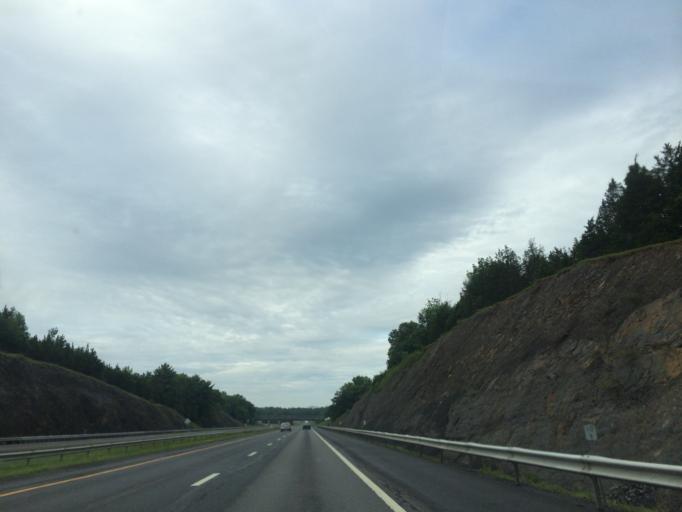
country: US
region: New York
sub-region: Greene County
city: Jefferson Heights
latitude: 42.2402
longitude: -73.8971
